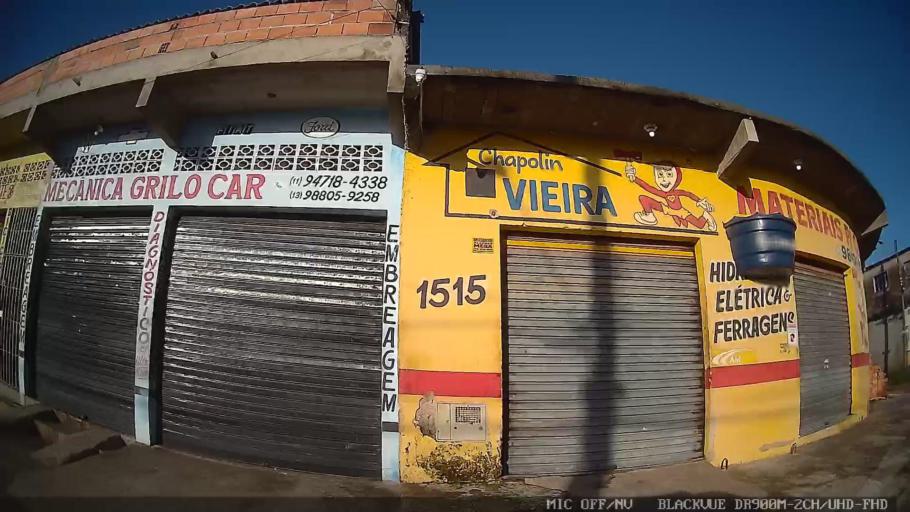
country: BR
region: Sao Paulo
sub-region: Itanhaem
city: Itanhaem
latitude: -24.2337
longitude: -46.9037
